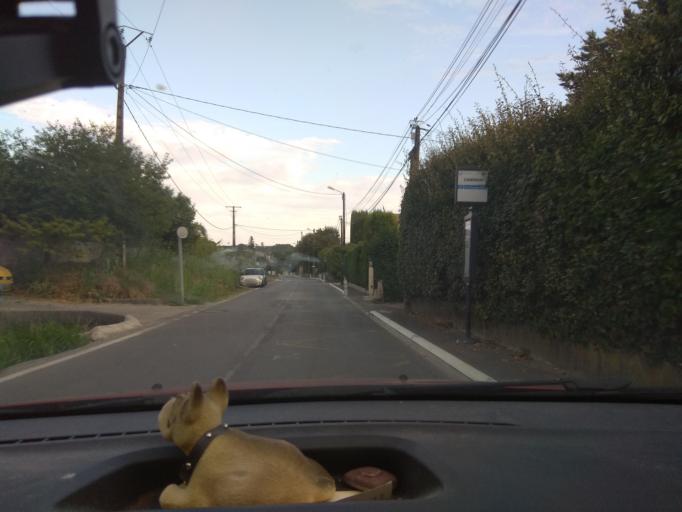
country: FR
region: Provence-Alpes-Cote d'Azur
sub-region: Departement des Alpes-Maritimes
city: La Colle-sur-Loup
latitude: 43.6780
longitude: 7.1078
